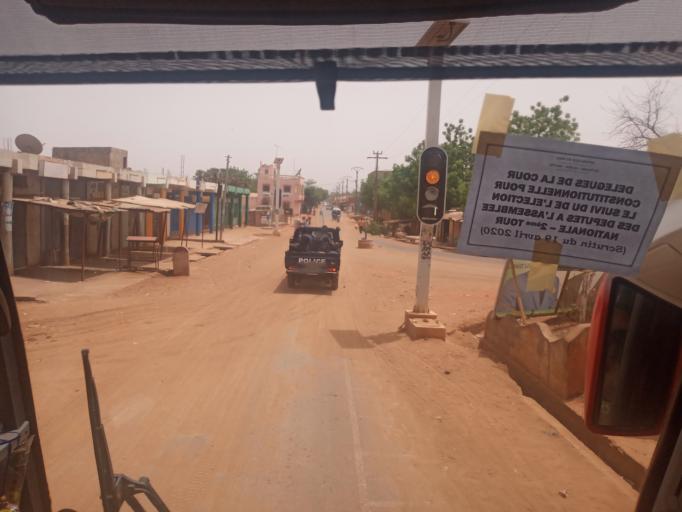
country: ML
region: Koulikoro
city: Koulikoro
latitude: 12.8923
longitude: -7.5406
